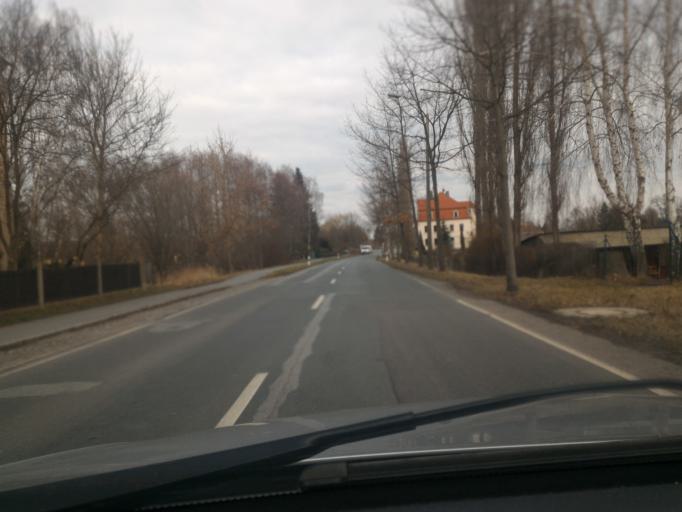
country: DE
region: Saxony
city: Zittau
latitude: 50.8751
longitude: 14.8106
